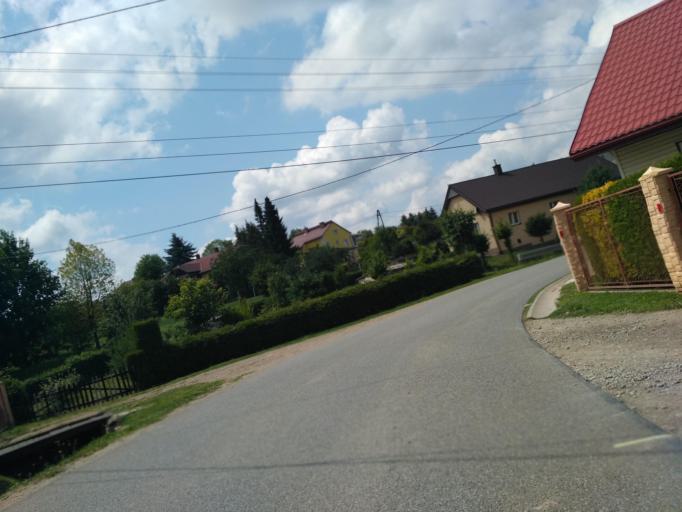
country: PL
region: Subcarpathian Voivodeship
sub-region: Powiat krosnienski
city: Dukla
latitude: 49.5924
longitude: 21.7222
